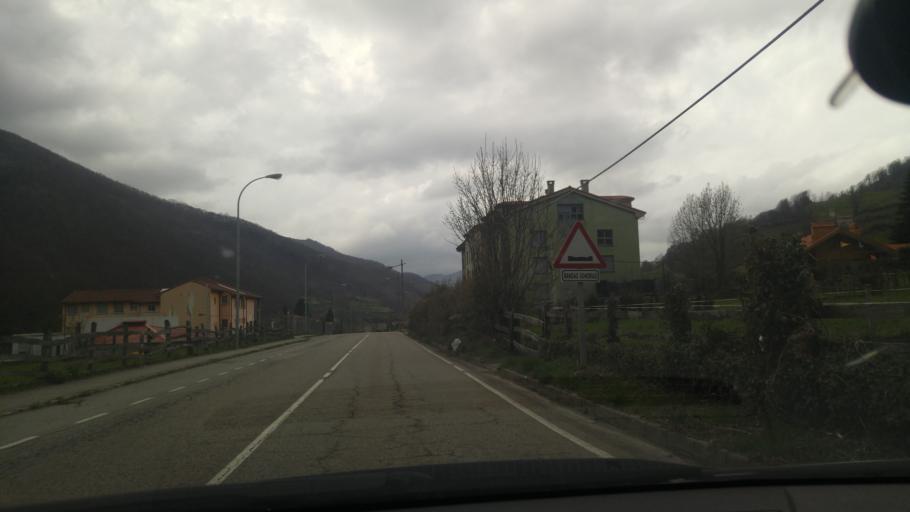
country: ES
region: Asturias
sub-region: Province of Asturias
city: Rio Aller
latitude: 43.1056
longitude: -5.5131
